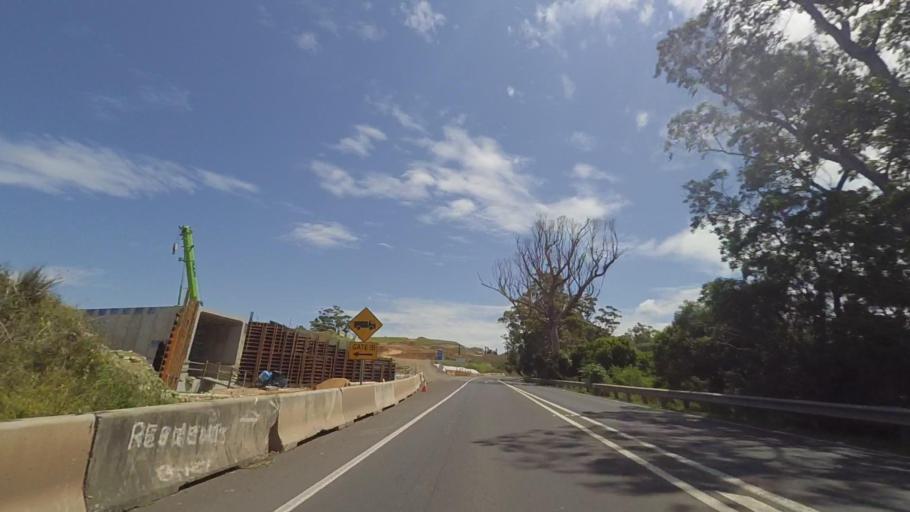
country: AU
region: New South Wales
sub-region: Kiama
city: Gerringong
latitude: -34.7477
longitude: 150.7757
